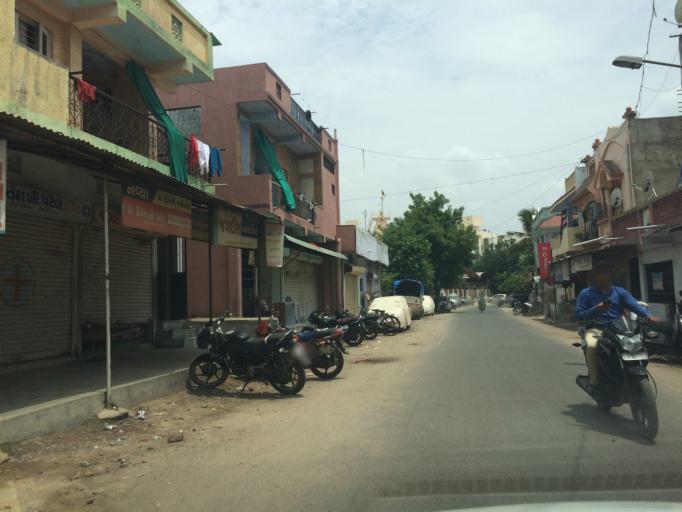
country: IN
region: Gujarat
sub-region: Ahmadabad
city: Ahmedabad
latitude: 23.0773
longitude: 72.5645
